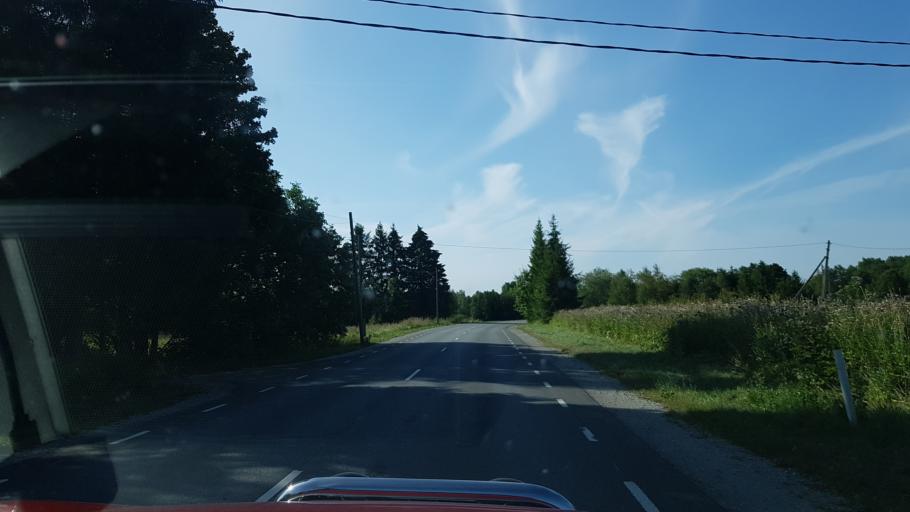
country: EE
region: Harju
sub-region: Rae vald
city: Jueri
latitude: 59.3795
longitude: 24.9278
